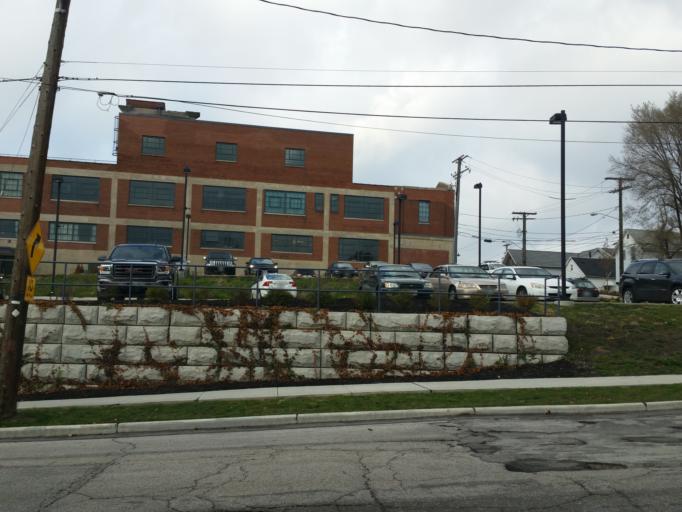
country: US
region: Ohio
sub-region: Cuyahoga County
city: Cleveland
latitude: 41.4798
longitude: -81.6960
